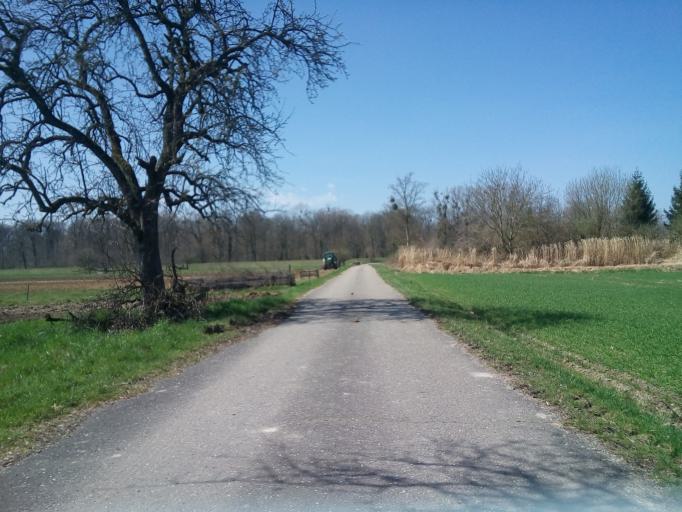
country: DE
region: Baden-Wuerttemberg
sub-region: Freiburg Region
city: Rheinau
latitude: 48.6691
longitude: 7.9215
